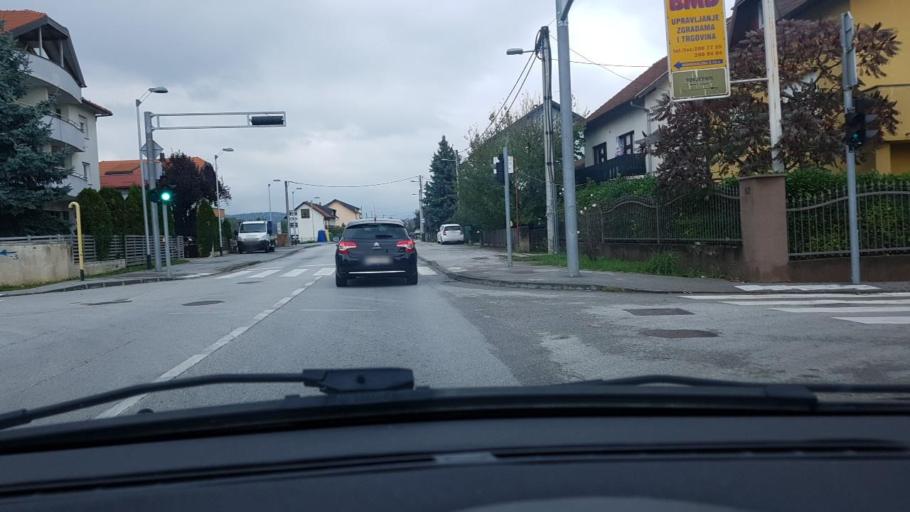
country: HR
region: Grad Zagreb
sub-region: Sesvete
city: Sesvete
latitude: 45.8540
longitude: 16.1127
